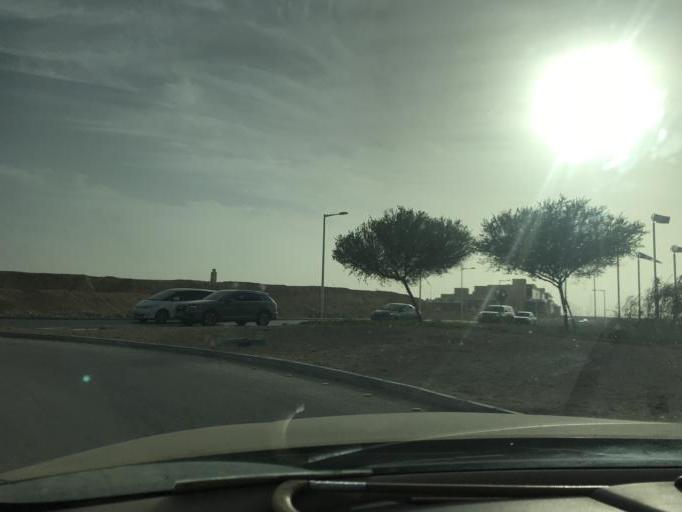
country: SA
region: Ar Riyad
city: Riyadh
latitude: 24.7350
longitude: 46.7414
